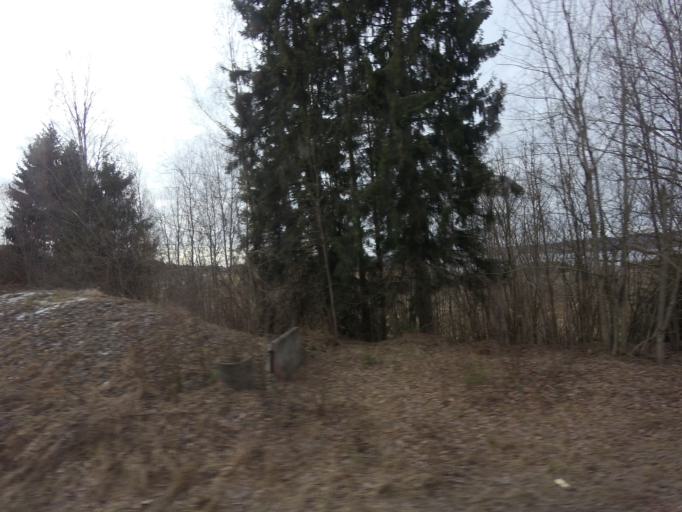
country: NO
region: Akershus
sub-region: Enebakk
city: Flateby
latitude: 59.8059
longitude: 11.2555
